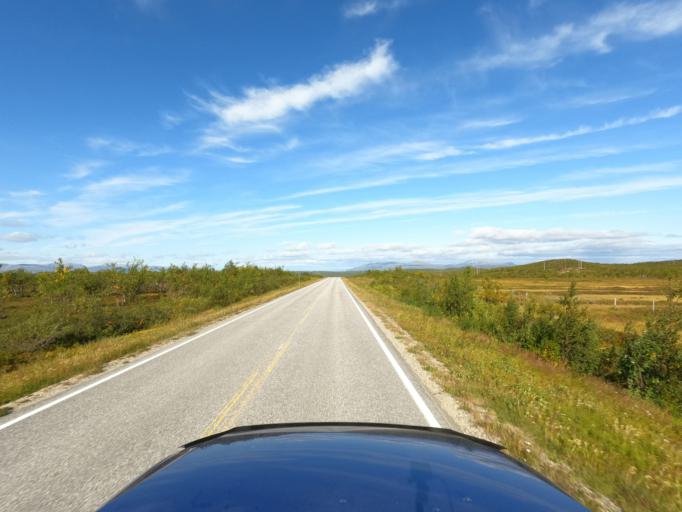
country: NO
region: Finnmark Fylke
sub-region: Karasjok
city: Karasjohka
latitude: 69.7209
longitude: 25.2375
